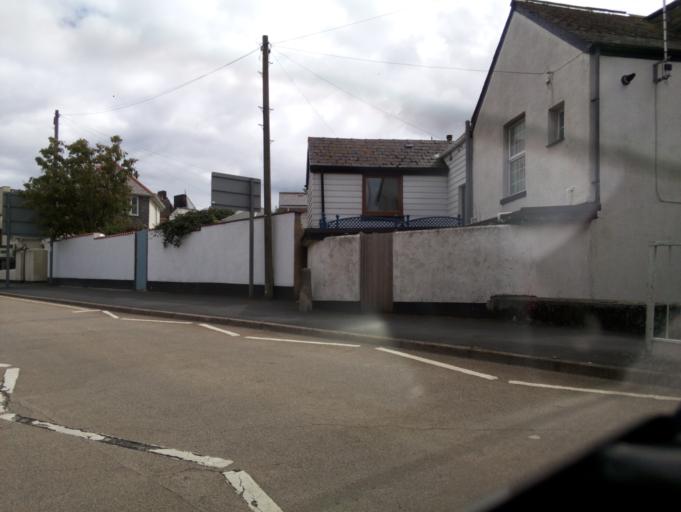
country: GB
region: England
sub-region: Devon
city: Teignmouth
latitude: 50.5476
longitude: -3.4934
